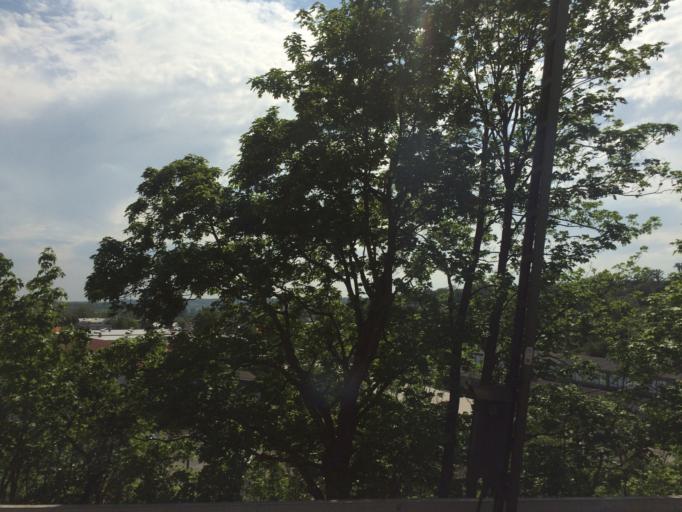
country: DE
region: Bavaria
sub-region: Regierungsbezirk Unterfranken
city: Kitzingen
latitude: 49.7275
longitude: 10.1590
